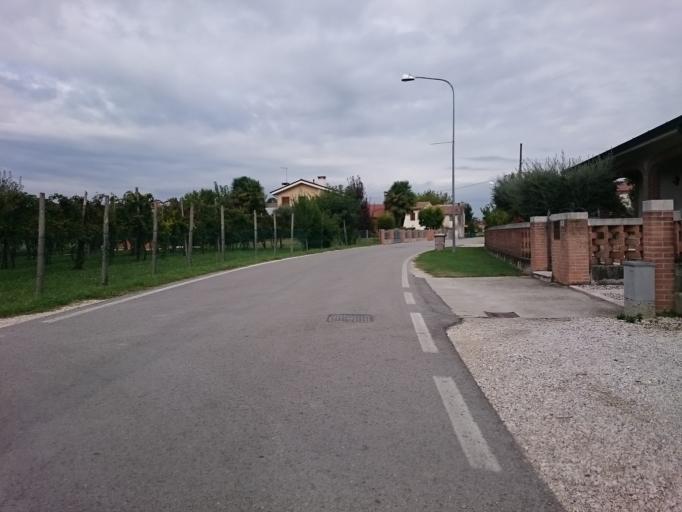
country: IT
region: Veneto
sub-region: Provincia di Vicenza
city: Grumolo delle Abbadesse
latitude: 45.4958
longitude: 11.6700
